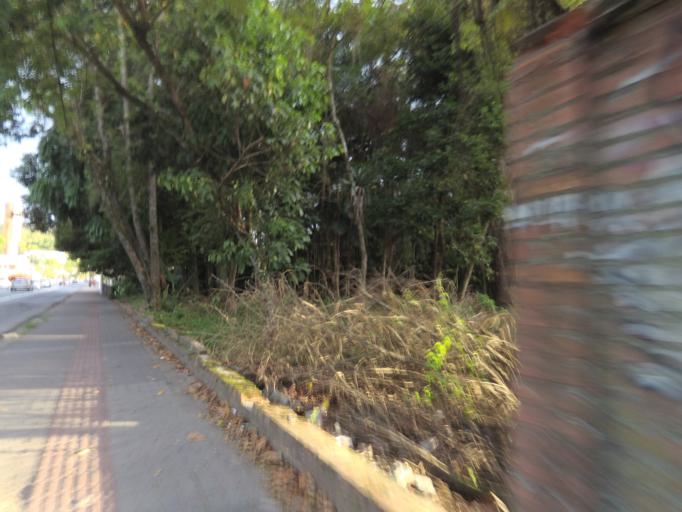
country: BR
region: Santa Catarina
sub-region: Blumenau
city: Blumenau
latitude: -26.9241
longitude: -49.0595
